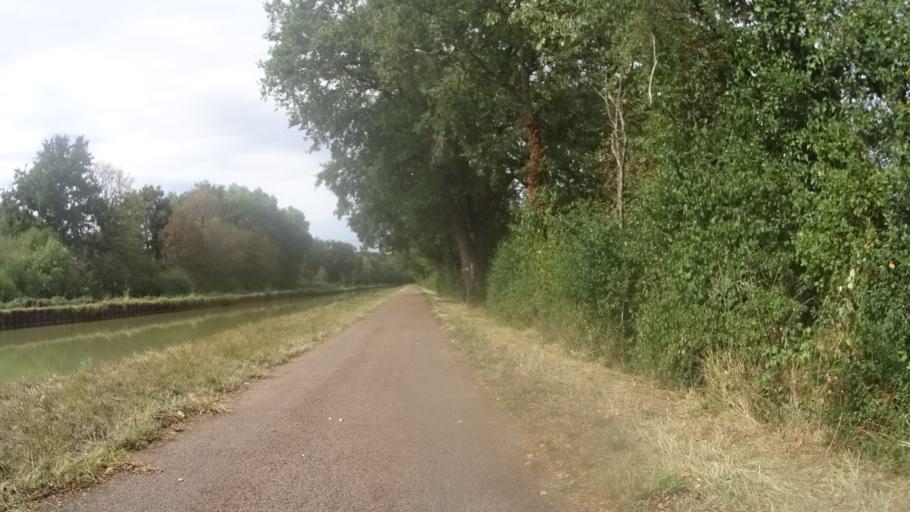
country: FR
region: Bourgogne
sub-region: Departement de la Nievre
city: Sermoise-sur-Loire
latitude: 46.9482
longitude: 3.2022
